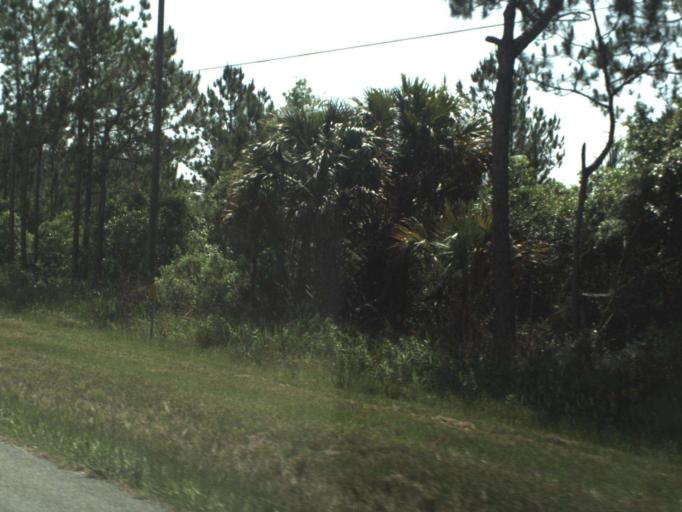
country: US
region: Florida
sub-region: Volusia County
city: North DeLand
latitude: 29.1033
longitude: -81.2105
